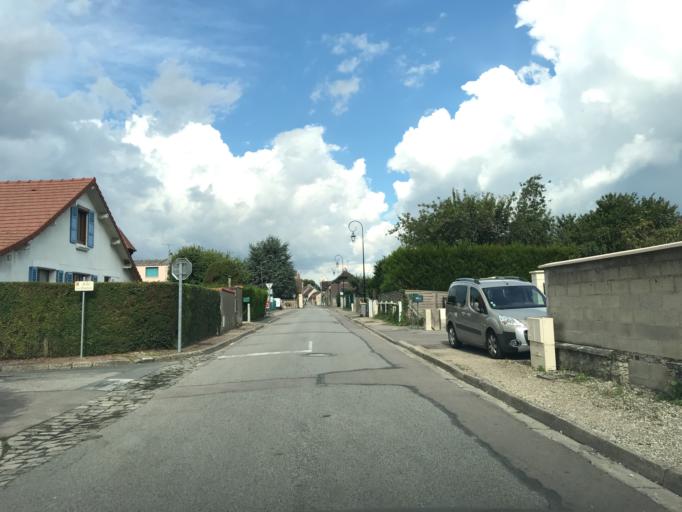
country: FR
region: Haute-Normandie
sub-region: Departement de l'Eure
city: Gasny
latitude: 49.0875
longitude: 1.5951
